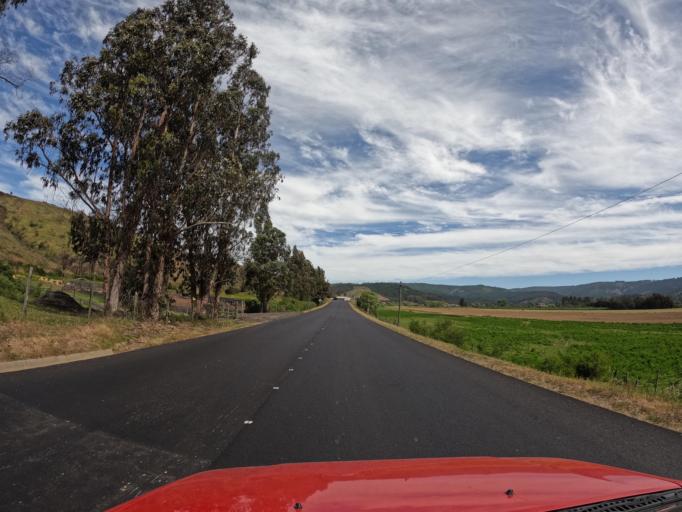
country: CL
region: Maule
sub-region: Provincia de Talca
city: Constitucion
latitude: -35.0736
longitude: -72.0397
